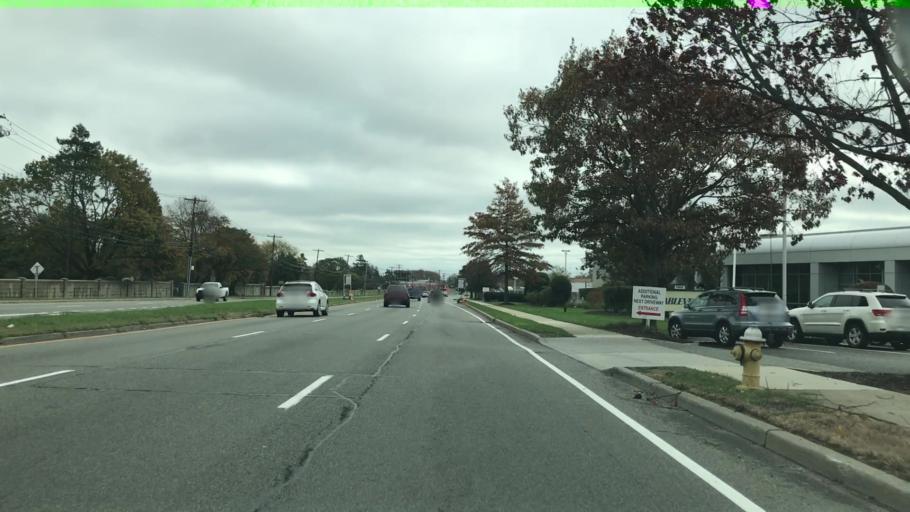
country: US
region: New York
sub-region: Suffolk County
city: North Lindenhurst
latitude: 40.7172
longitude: -73.4011
